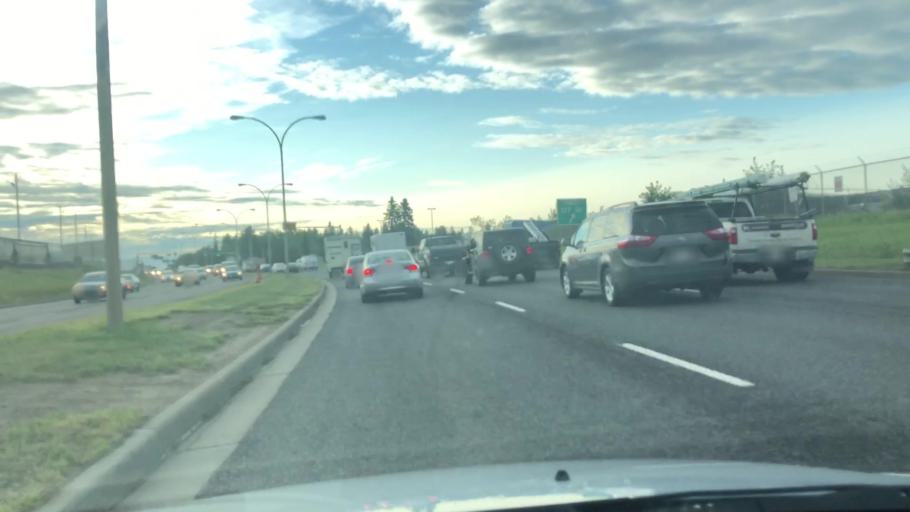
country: CA
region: Alberta
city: Edmonton
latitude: 53.5815
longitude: -113.5096
